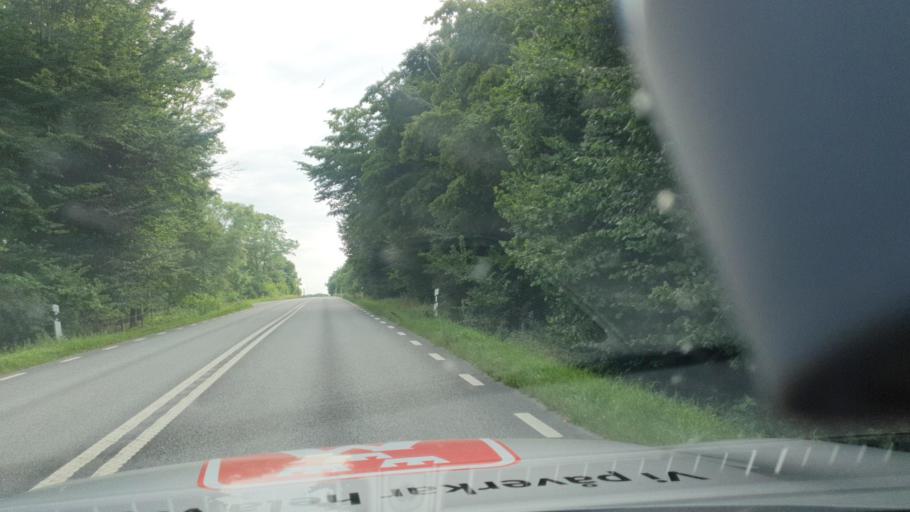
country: SE
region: Skane
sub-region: Bromolla Kommun
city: Bromoella
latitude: 56.1109
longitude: 14.5125
